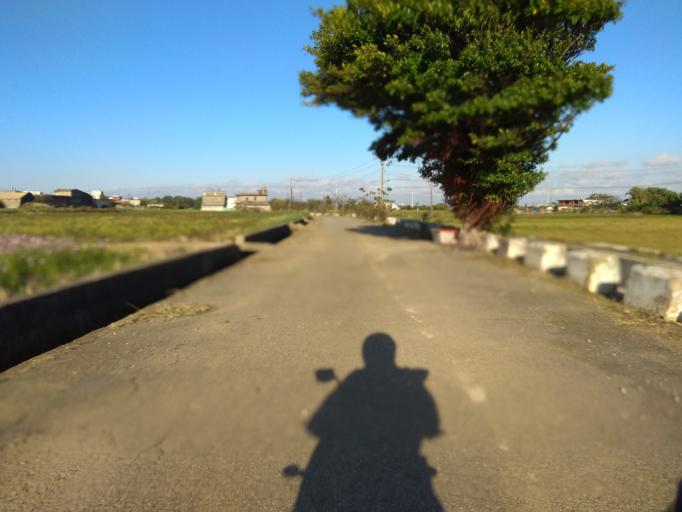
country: TW
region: Taiwan
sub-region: Hsinchu
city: Zhubei
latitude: 24.9863
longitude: 121.0531
